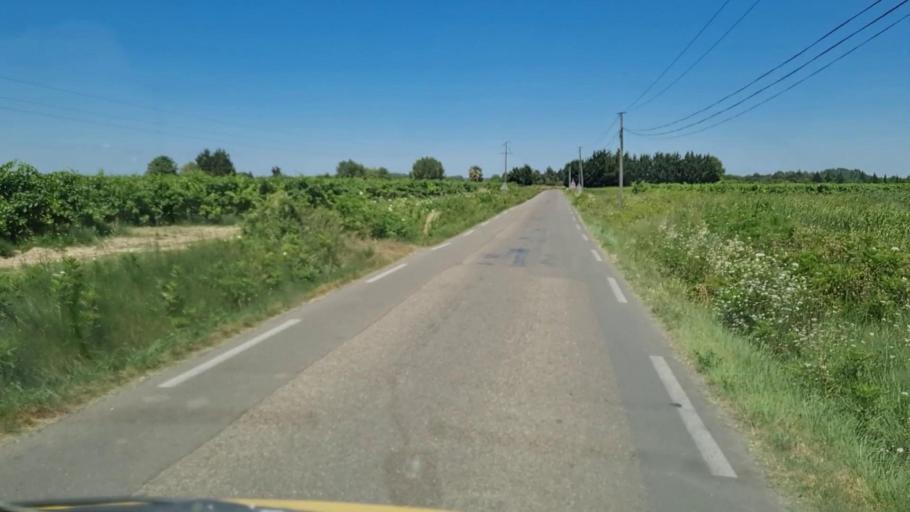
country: FR
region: Languedoc-Roussillon
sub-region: Departement de l'Herault
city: Marsillargues
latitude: 43.6706
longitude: 4.1847
